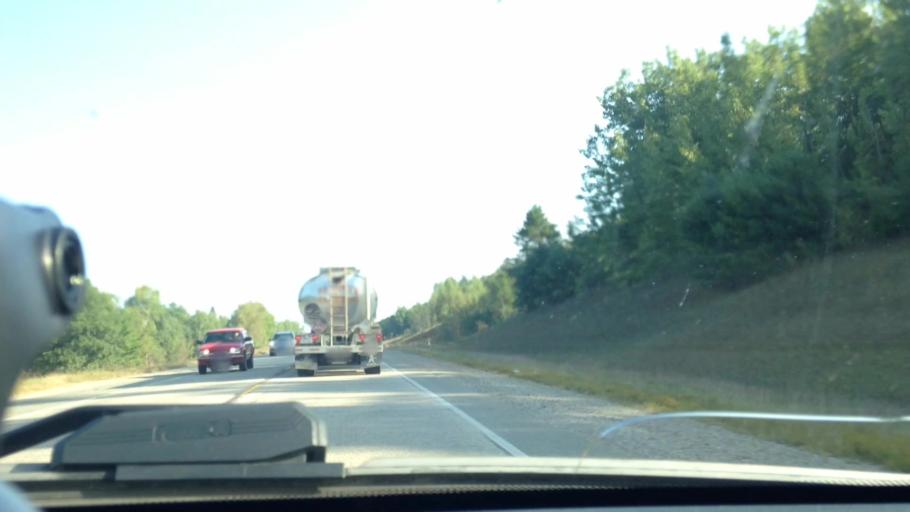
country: US
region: Wisconsin
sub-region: Marinette County
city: Niagara
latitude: 45.6508
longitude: -87.9640
